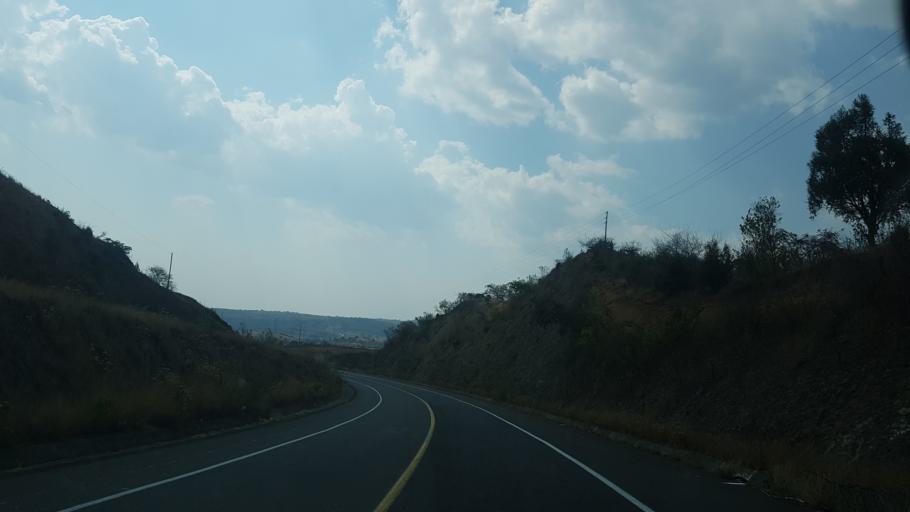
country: MX
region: Puebla
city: San Juan Amecac
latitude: 18.8216
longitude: -98.6850
